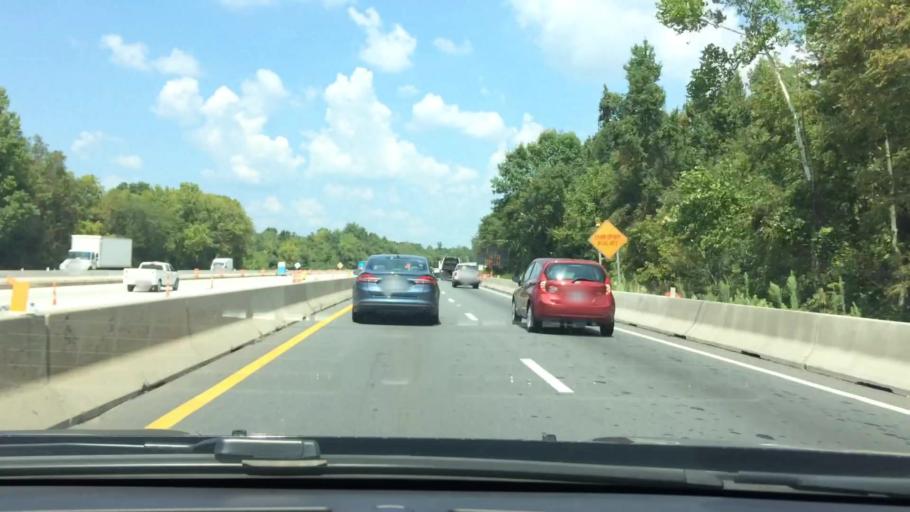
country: US
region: North Carolina
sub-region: Rowan County
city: China Grove
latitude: 35.5538
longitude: -80.5703
